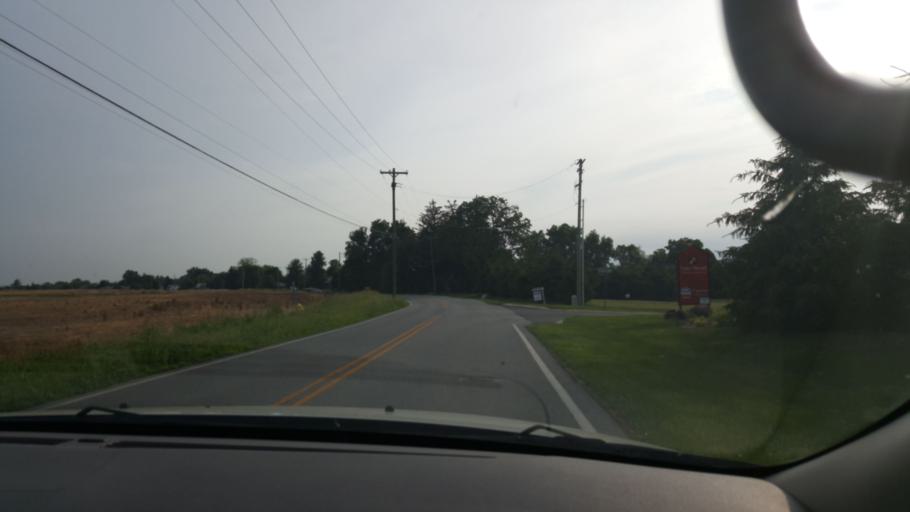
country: US
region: Pennsylvania
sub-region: York County
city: Weigelstown
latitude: 40.0019
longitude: -76.8067
